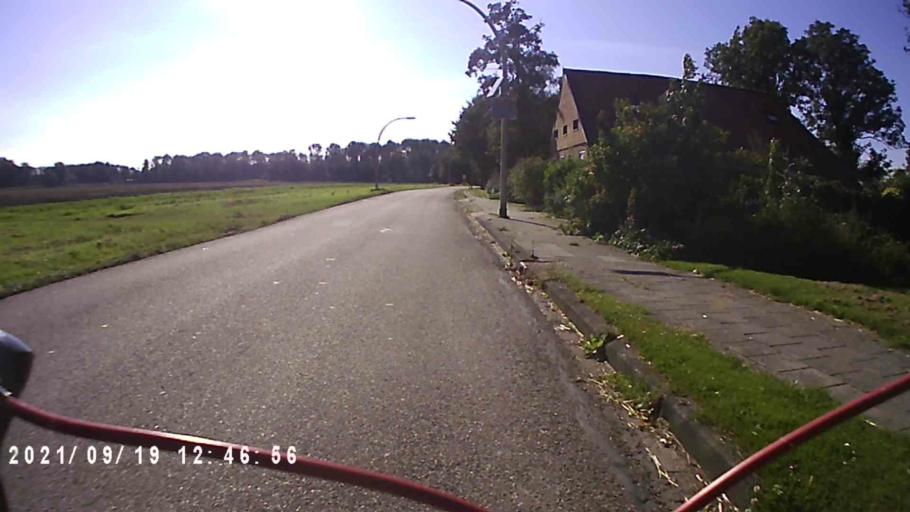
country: NL
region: Groningen
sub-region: Gemeente  Oldambt
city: Winschoten
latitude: 53.2141
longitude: 6.9421
